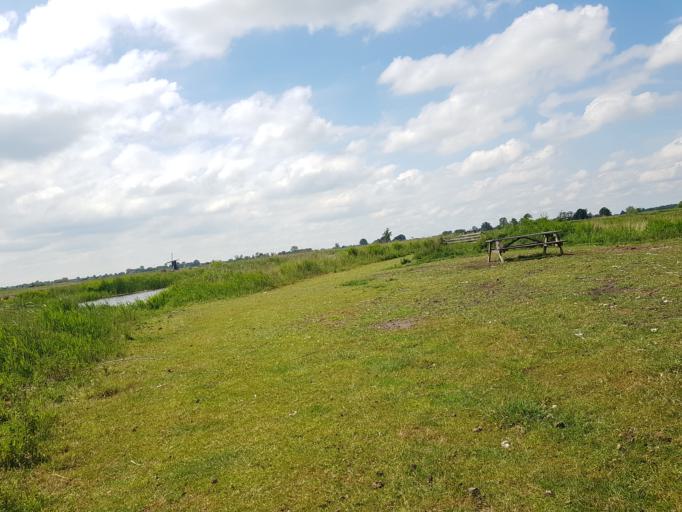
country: NL
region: Friesland
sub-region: Gemeente Boarnsterhim
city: Aldeboarn
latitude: 53.0942
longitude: 5.9011
